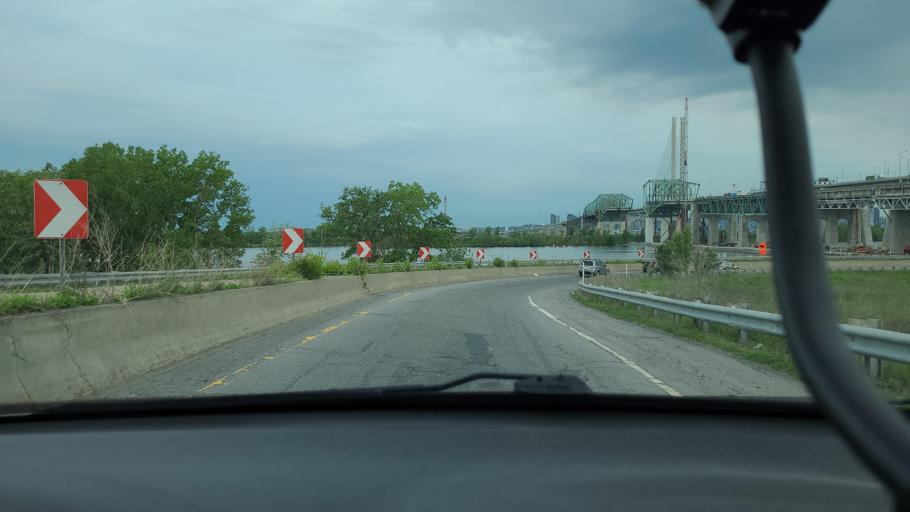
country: CA
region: Quebec
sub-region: Monteregie
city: Brossard
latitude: 45.4649
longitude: -73.4946
